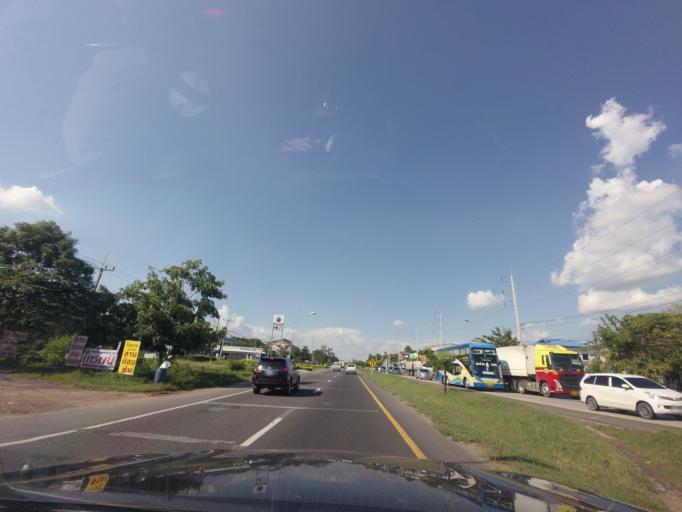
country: TH
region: Nakhon Ratchasima
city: Sida
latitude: 15.5494
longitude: 102.5482
